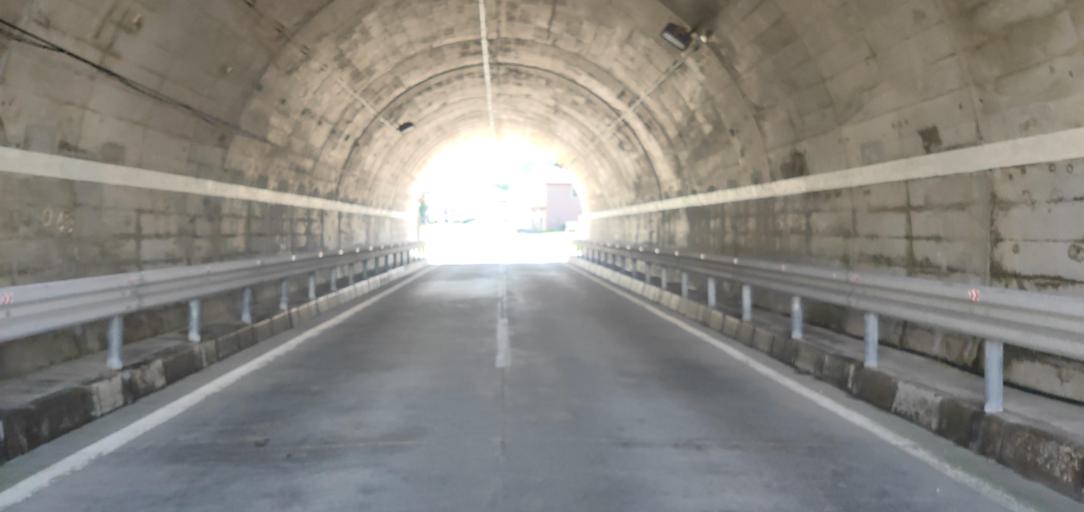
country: JP
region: Hokkaido
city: Shibetsu
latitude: 44.0739
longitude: 144.9914
